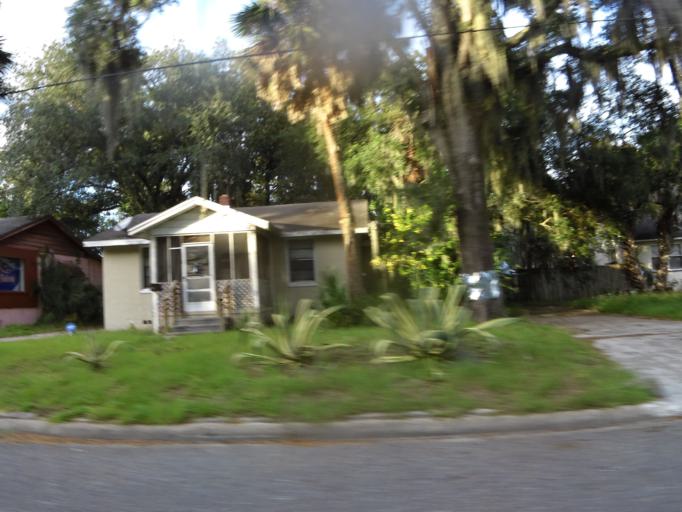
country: US
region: Florida
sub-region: Duval County
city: Jacksonville
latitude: 30.3687
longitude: -81.6554
